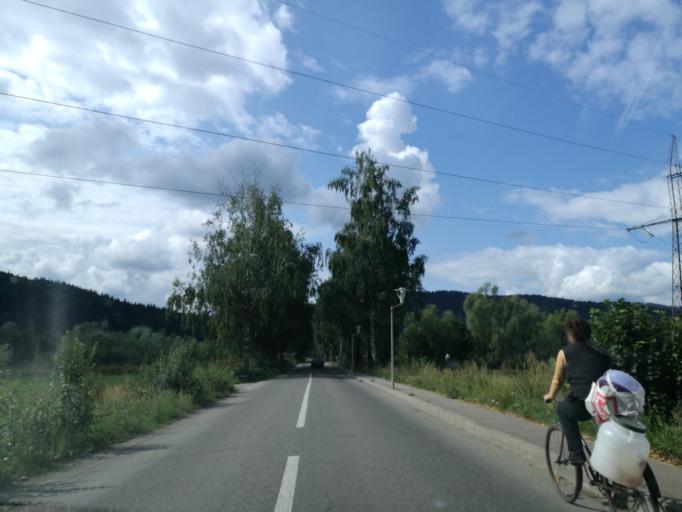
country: RO
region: Suceava
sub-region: Oras Gura Humorului
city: Gura Humorului
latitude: 47.5452
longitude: 25.8710
